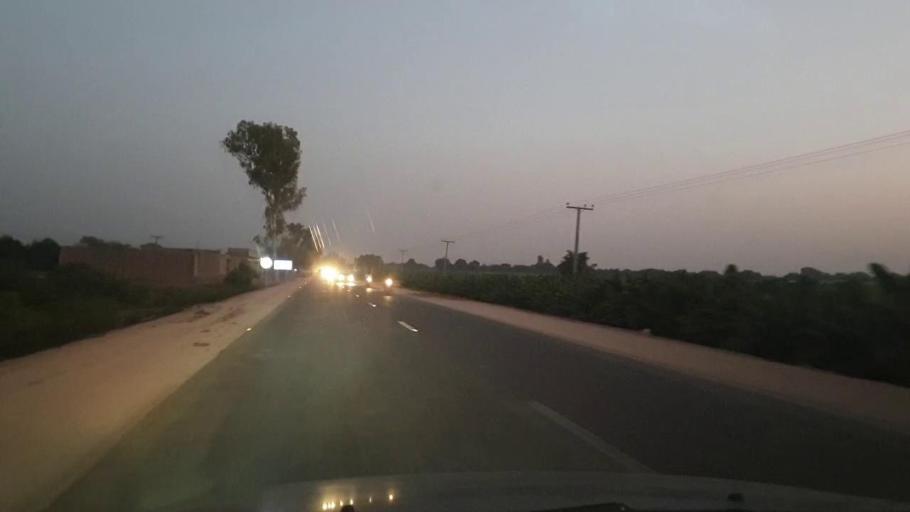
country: PK
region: Sindh
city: Tando Allahyar
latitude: 25.4090
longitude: 68.7575
